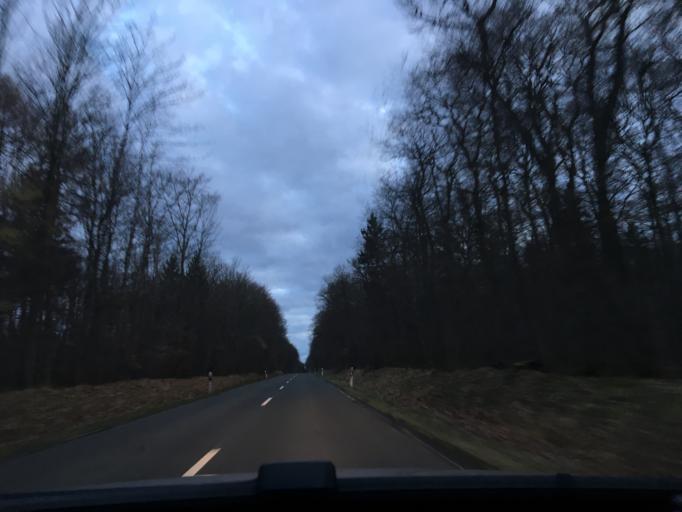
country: DE
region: Rheinland-Pfalz
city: Bechenheim
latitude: 49.7198
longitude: 8.0019
